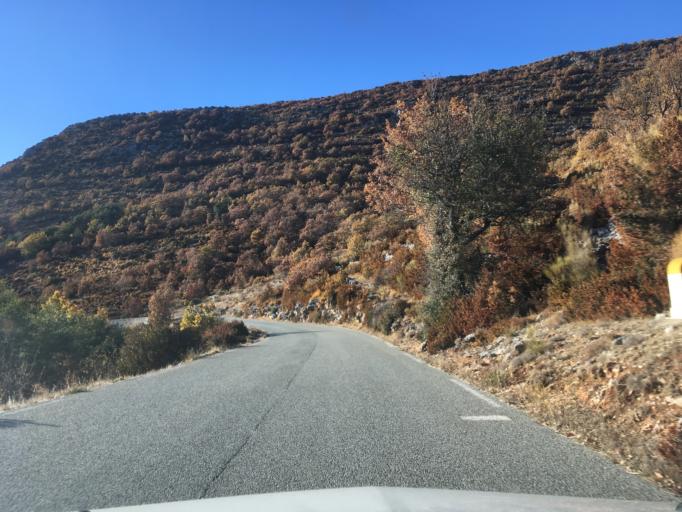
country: FR
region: Provence-Alpes-Cote d'Azur
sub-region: Departement des Alpes-de-Haute-Provence
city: Castellane
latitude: 43.7529
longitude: 6.4048
